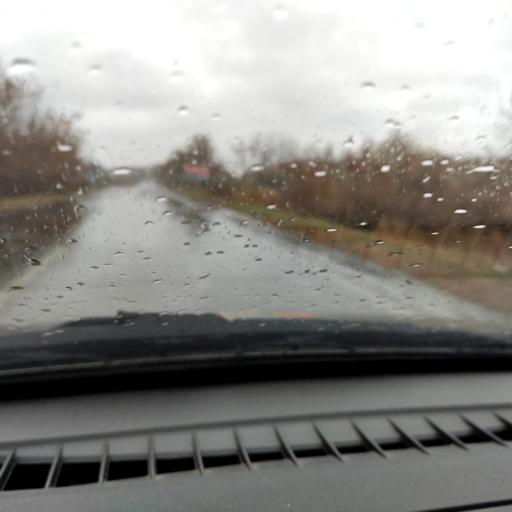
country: RU
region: Samara
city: Tol'yatti
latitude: 53.6526
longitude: 49.2907
